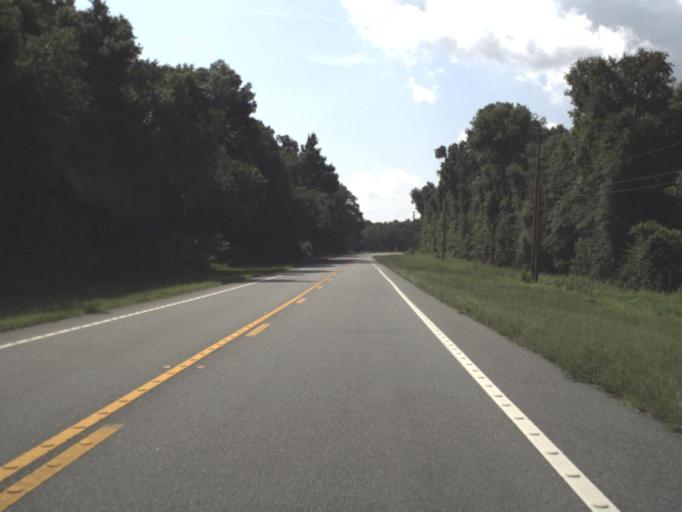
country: US
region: Florida
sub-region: Citrus County
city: Hernando
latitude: 28.9131
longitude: -82.3834
